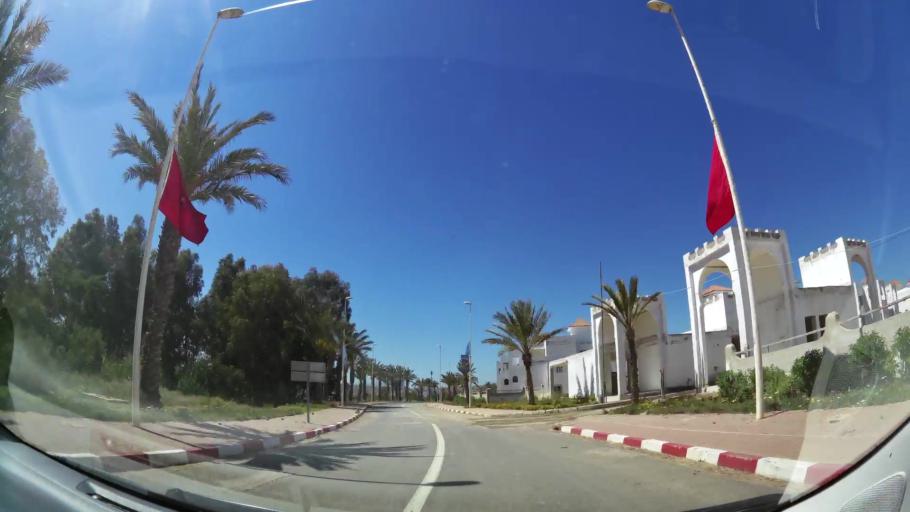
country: MA
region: Oriental
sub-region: Berkane-Taourirt
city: Madagh
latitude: 35.1099
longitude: -2.3105
